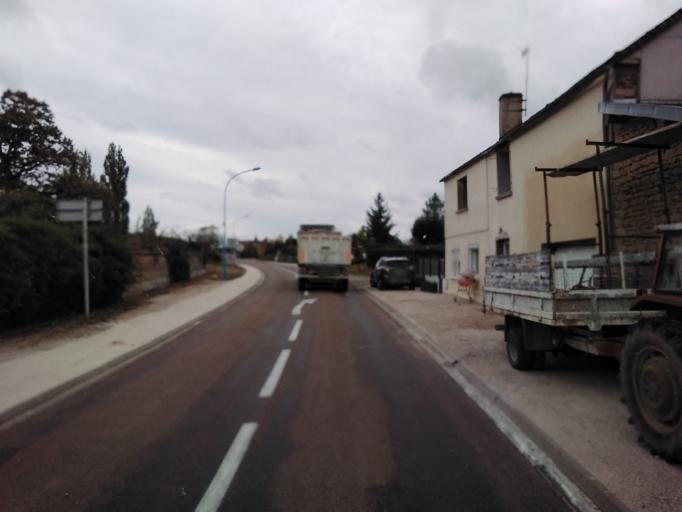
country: FR
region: Champagne-Ardenne
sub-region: Departement de l'Aube
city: Vendeuvre-sur-Barse
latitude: 48.2926
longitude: 4.5154
